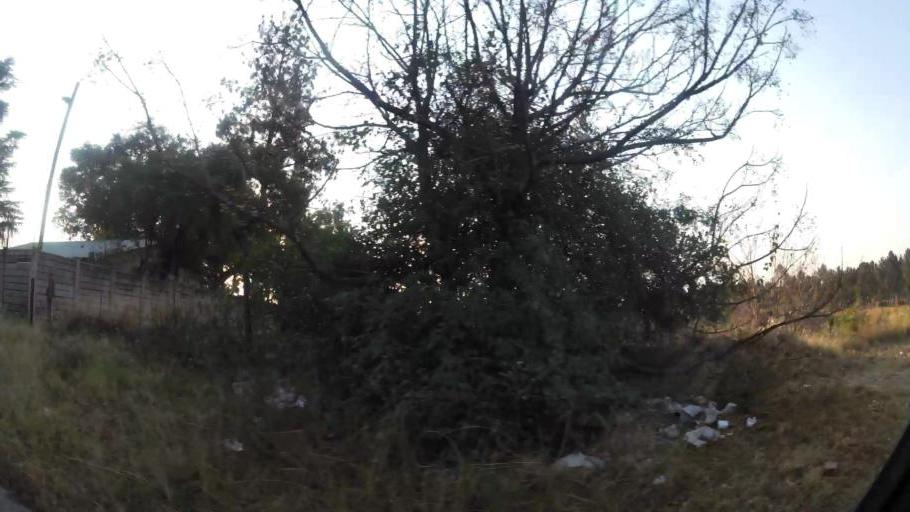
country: ZA
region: Gauteng
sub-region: City of Johannesburg Metropolitan Municipality
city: Diepsloot
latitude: -26.0043
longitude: 27.9902
